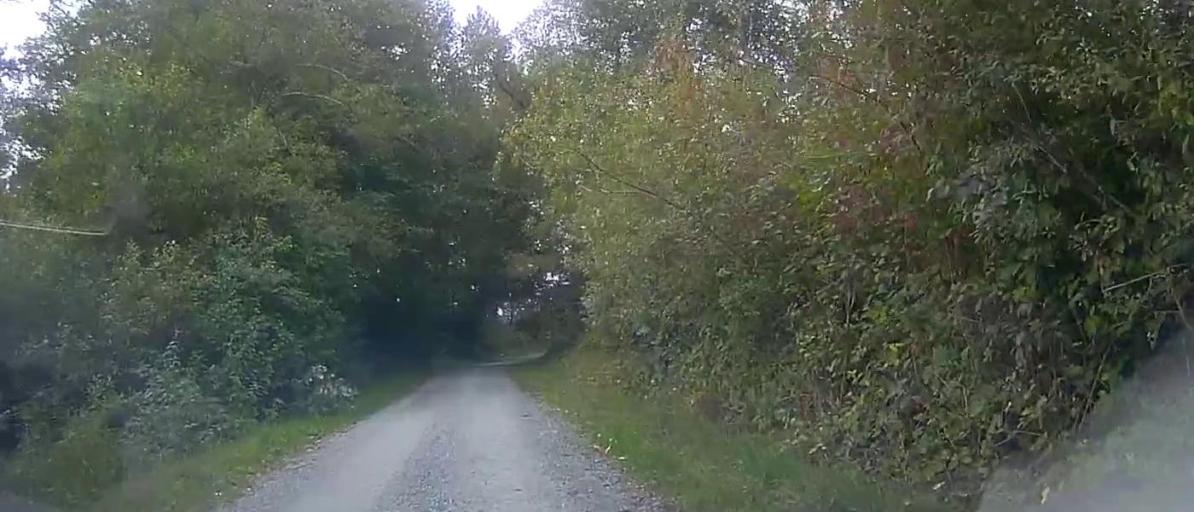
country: US
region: Washington
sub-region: Skagit County
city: Clear Lake
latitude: 48.4681
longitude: -122.2563
